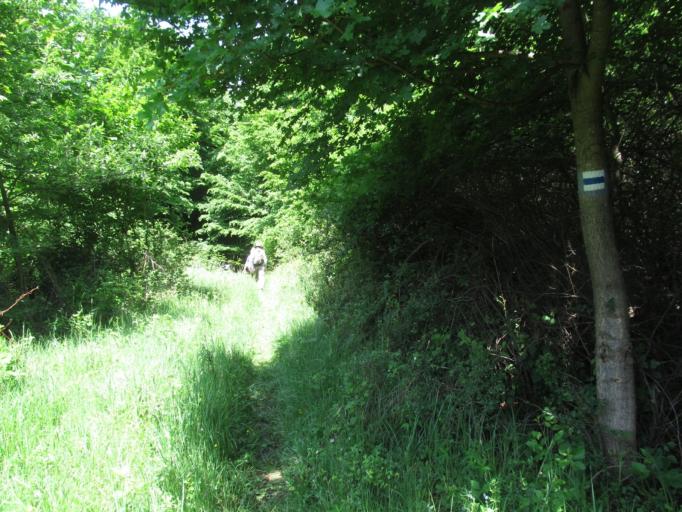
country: HU
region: Borsod-Abauj-Zemplen
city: Gonc
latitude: 48.5543
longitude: 21.4226
